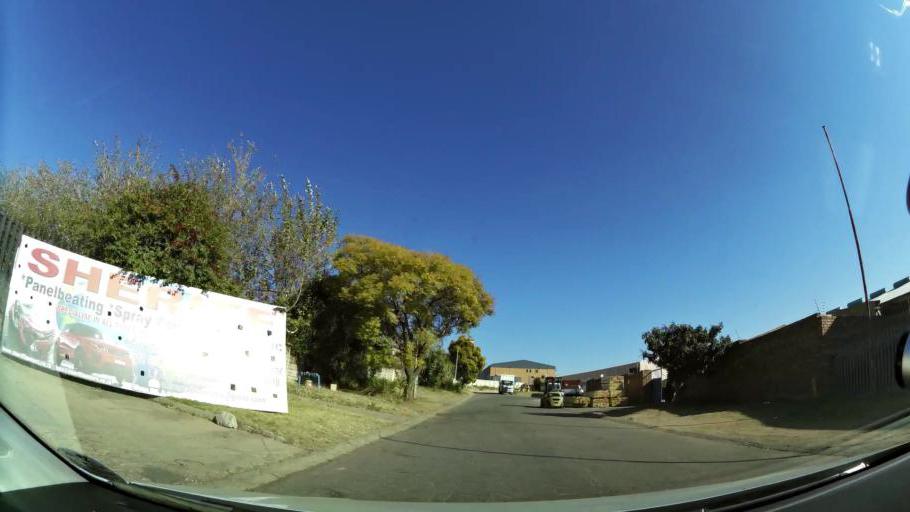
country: ZA
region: Gauteng
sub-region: City of Johannesburg Metropolitan Municipality
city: Modderfontein
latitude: -26.0646
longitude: 28.1952
